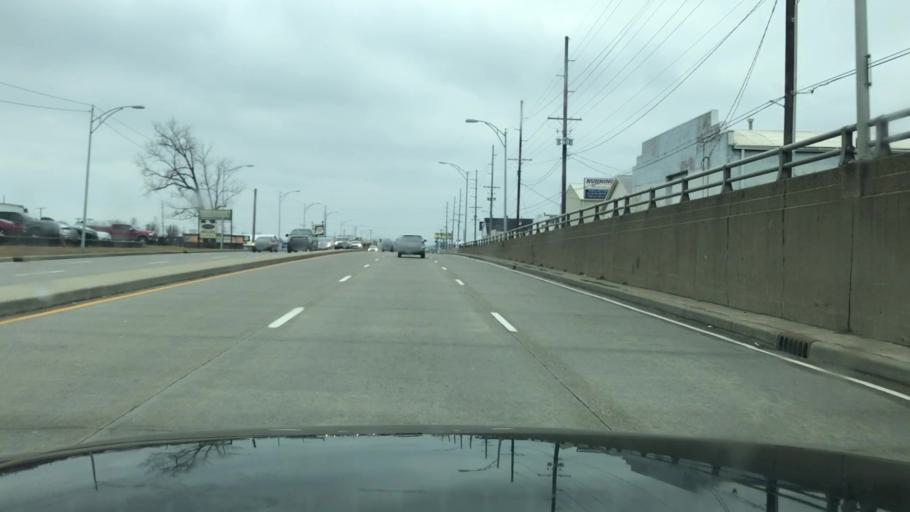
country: US
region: Indiana
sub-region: Vanderburgh County
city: Evansville
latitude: 37.9992
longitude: -87.5432
